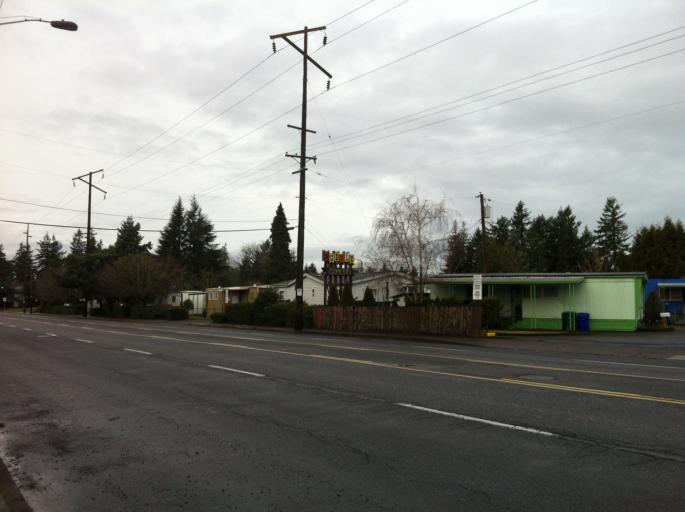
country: US
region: Oregon
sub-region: Multnomah County
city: Lents
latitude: 45.5190
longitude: -122.5280
